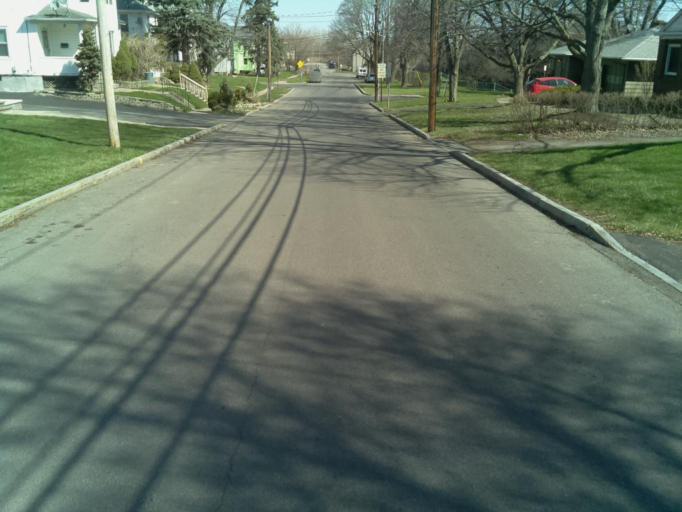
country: US
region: New York
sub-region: Onondaga County
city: East Syracuse
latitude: 43.0704
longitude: -76.1000
